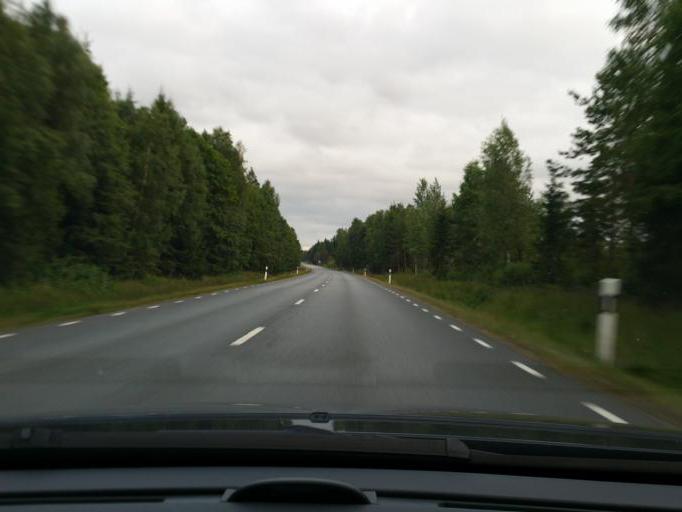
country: SE
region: Kronoberg
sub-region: Alvesta Kommun
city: Moheda
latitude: 57.0089
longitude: 14.5583
